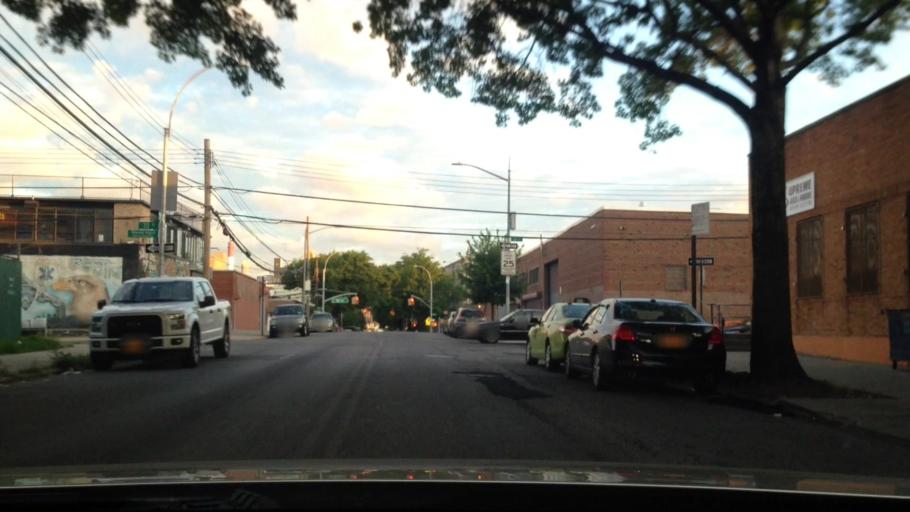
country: US
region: New York
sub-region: Queens County
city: Long Island City
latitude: 40.7552
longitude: -73.9314
